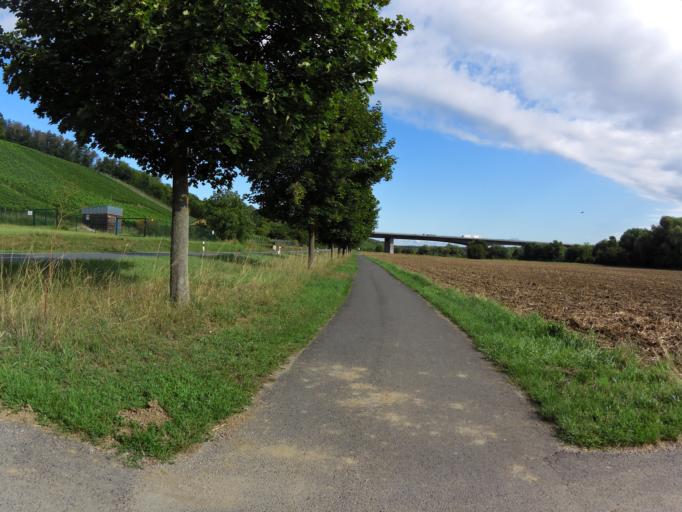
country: DE
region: Bavaria
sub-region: Regierungsbezirk Unterfranken
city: Mainstockheim
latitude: 49.7818
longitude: 10.1513
